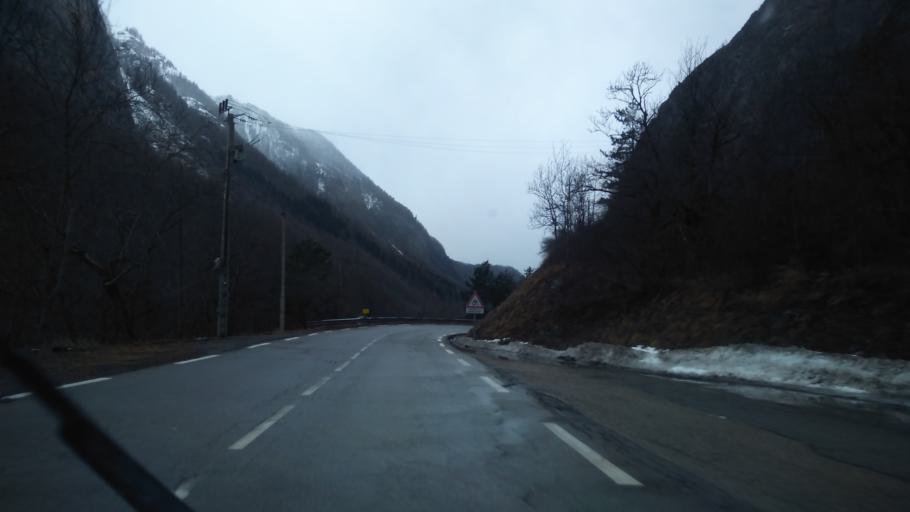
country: FR
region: Rhone-Alpes
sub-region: Departement de l'Isere
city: Mont-de-Lans
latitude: 45.0390
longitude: 6.1853
